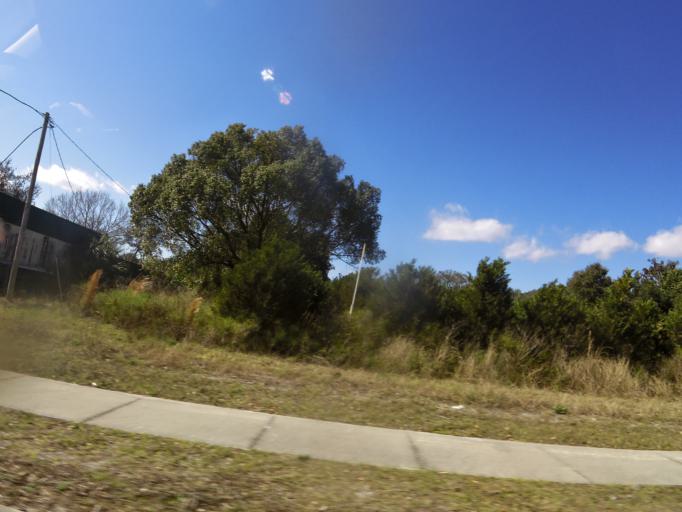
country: US
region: Florida
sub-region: Volusia County
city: Pierson
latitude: 29.2342
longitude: -81.4628
